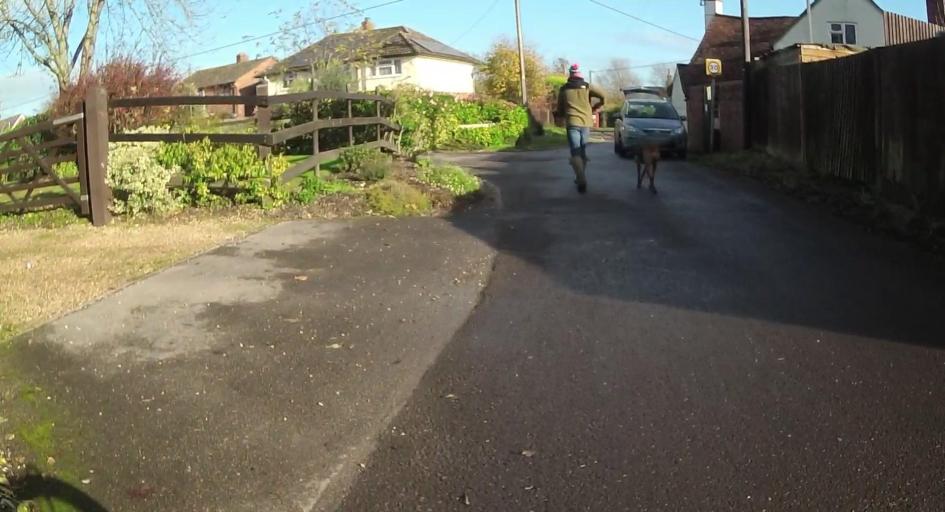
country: GB
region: England
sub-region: Wokingham
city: Swallowfield
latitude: 51.3642
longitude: -0.9652
